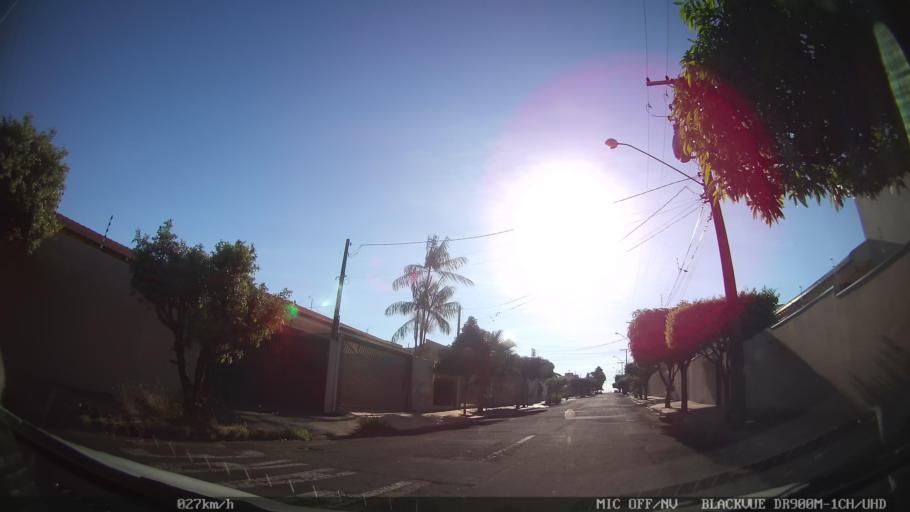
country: BR
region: Sao Paulo
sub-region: Sao Jose Do Rio Preto
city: Sao Jose do Rio Preto
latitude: -20.8228
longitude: -49.4098
